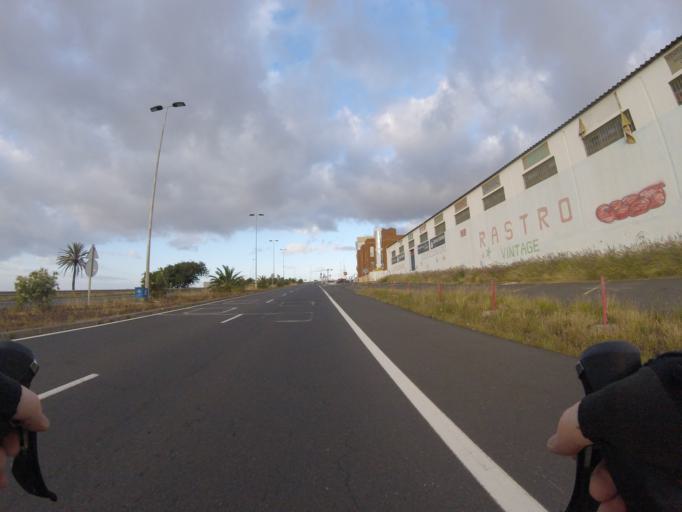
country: ES
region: Canary Islands
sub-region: Provincia de Santa Cruz de Tenerife
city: La Laguna
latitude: 28.4291
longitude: -16.3124
